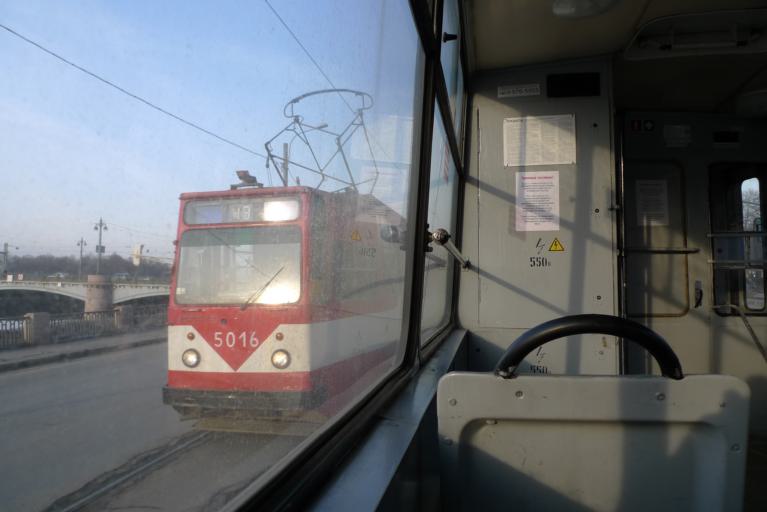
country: RU
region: Leningrad
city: Chernaya Rechka
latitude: 59.9763
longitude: 30.3010
